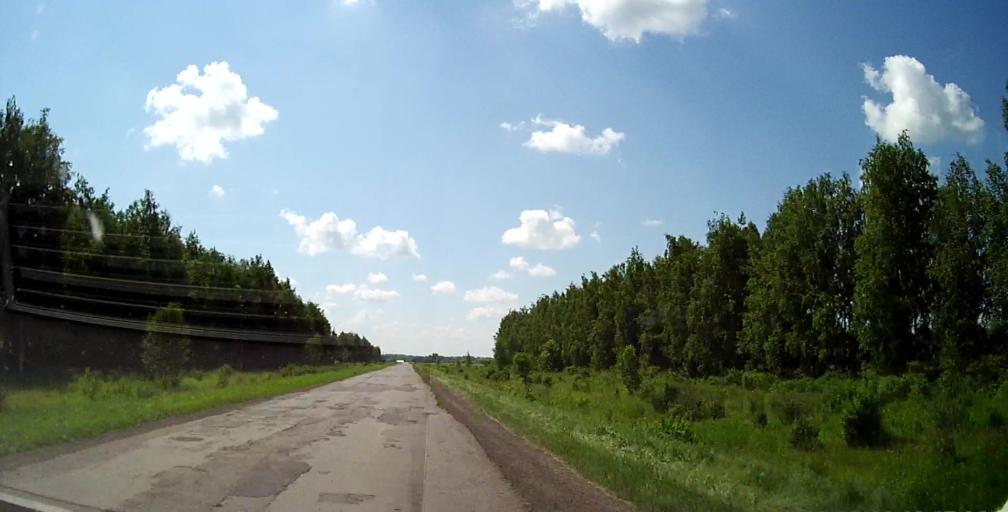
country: RU
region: Lipetsk
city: Chaplygin
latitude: 53.3611
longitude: 39.9206
